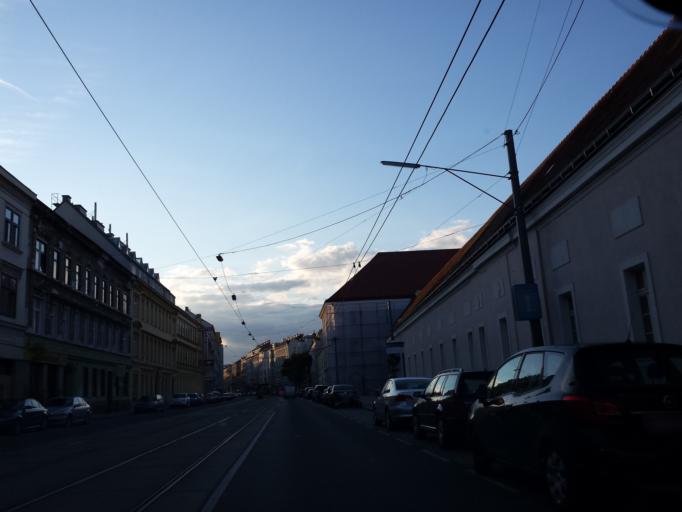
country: AT
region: Vienna
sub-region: Wien Stadt
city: Vienna
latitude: 48.1904
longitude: 16.3976
